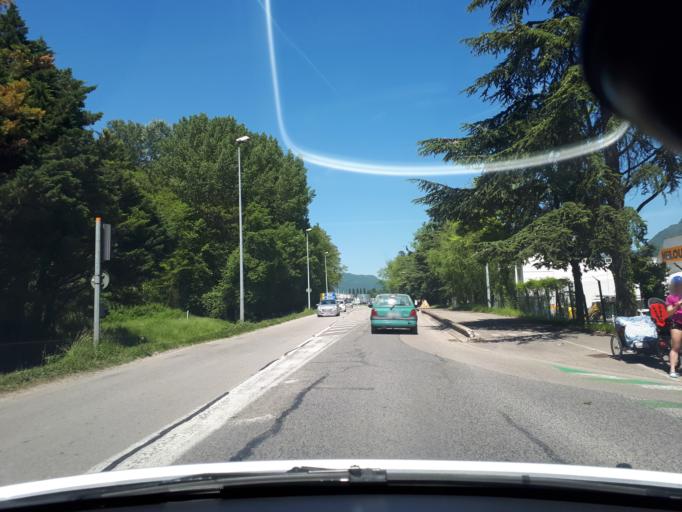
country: FR
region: Rhone-Alpes
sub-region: Departement de l'Isere
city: Fontanil-Cornillon
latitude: 45.2378
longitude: 5.6687
